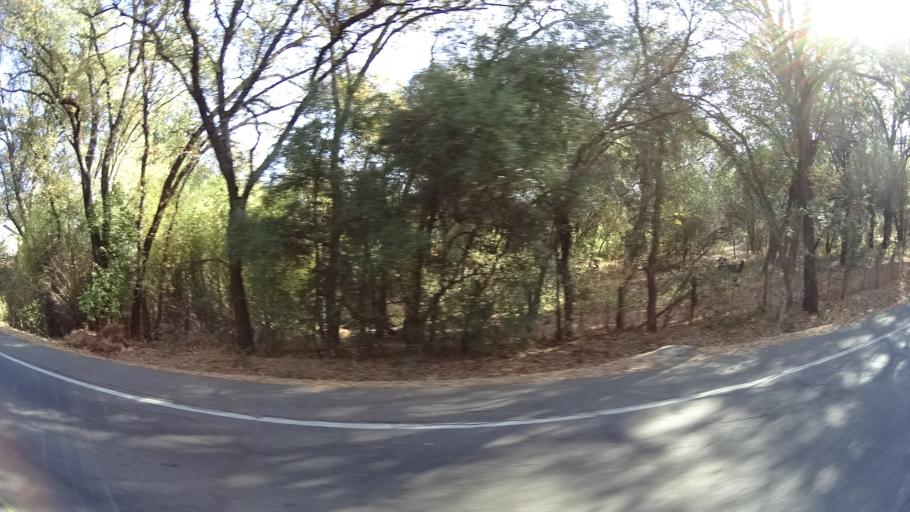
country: US
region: California
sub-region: Sacramento County
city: Citrus Heights
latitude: 38.6884
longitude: -121.2833
